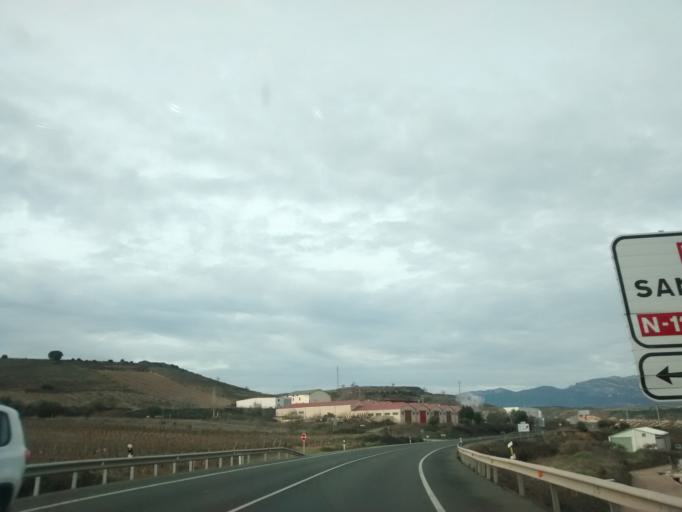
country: ES
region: La Rioja
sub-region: Provincia de La Rioja
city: Cenicero
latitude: 42.4733
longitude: -2.6427
